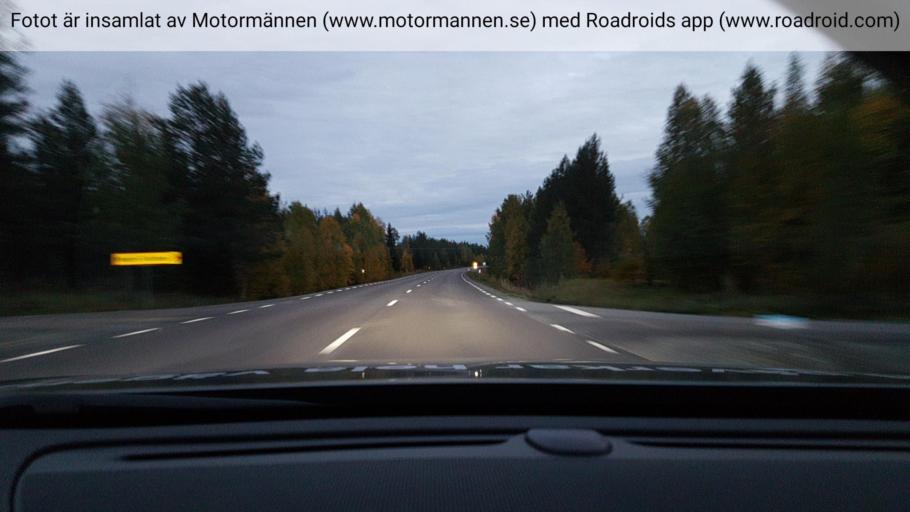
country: SE
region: Norrbotten
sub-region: Alvsbyns Kommun
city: AElvsbyn
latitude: 65.7341
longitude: 20.9775
